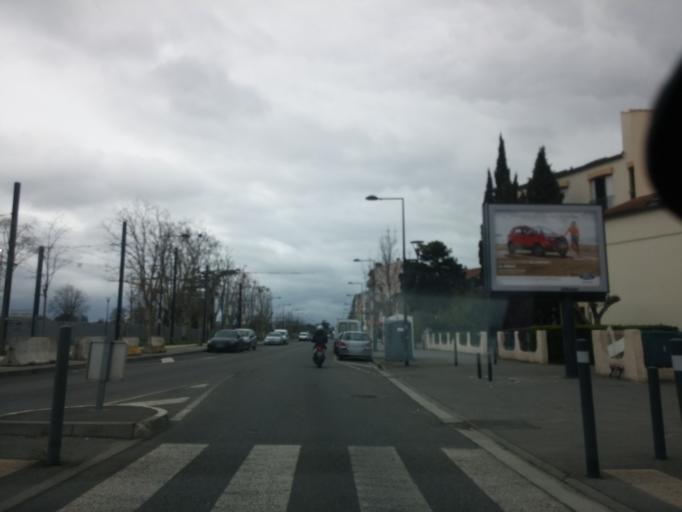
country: FR
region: Midi-Pyrenees
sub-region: Departement de la Haute-Garonne
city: Toulouse
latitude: 43.6016
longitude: 1.4116
